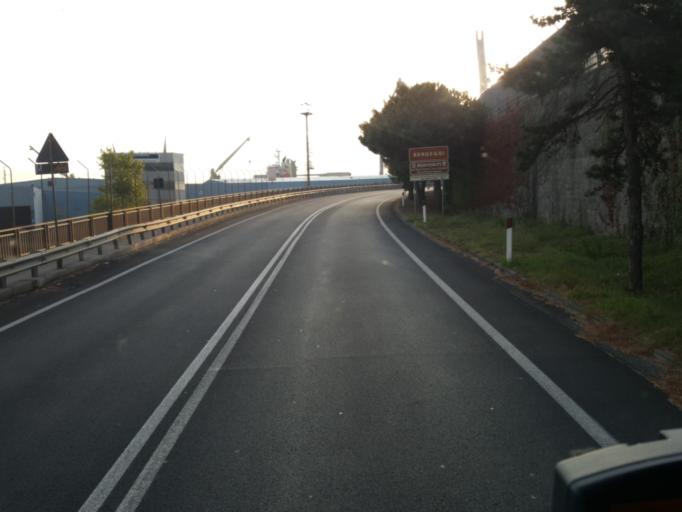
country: IT
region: Liguria
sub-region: Provincia di Savona
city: Bergeggi
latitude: 44.2617
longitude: 8.4488
